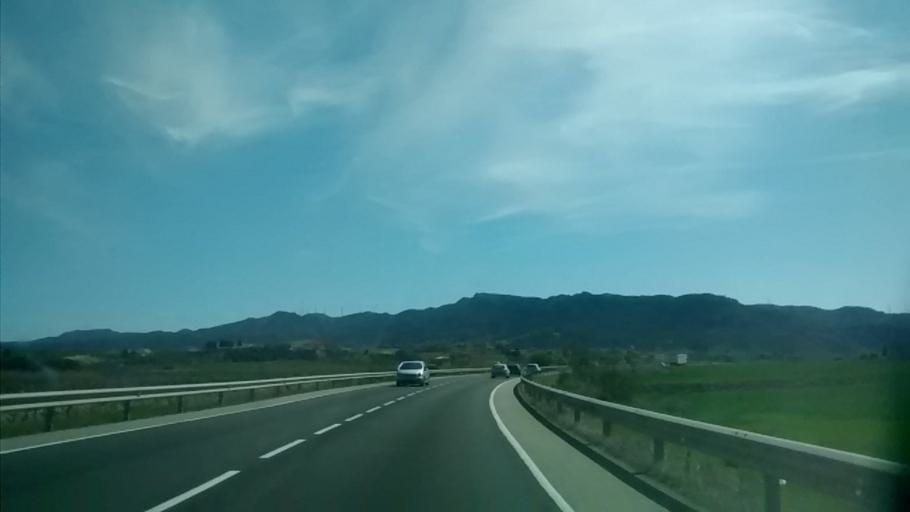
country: ES
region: Catalonia
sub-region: Provincia de Tarragona
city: Asco
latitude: 41.1872
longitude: 0.5746
